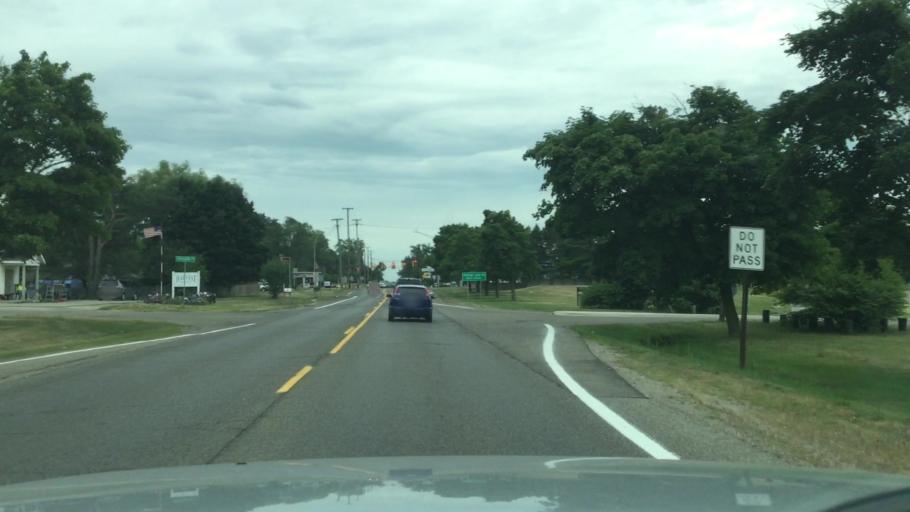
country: US
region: Michigan
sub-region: Oakland County
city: Keego Harbor
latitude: 42.6563
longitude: -83.3466
